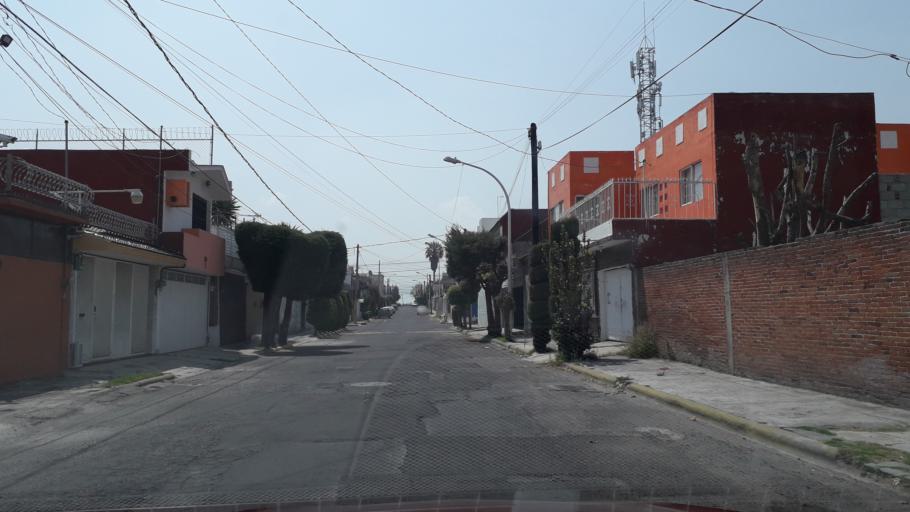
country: MX
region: Puebla
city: Puebla
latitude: 19.0590
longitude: -98.1791
